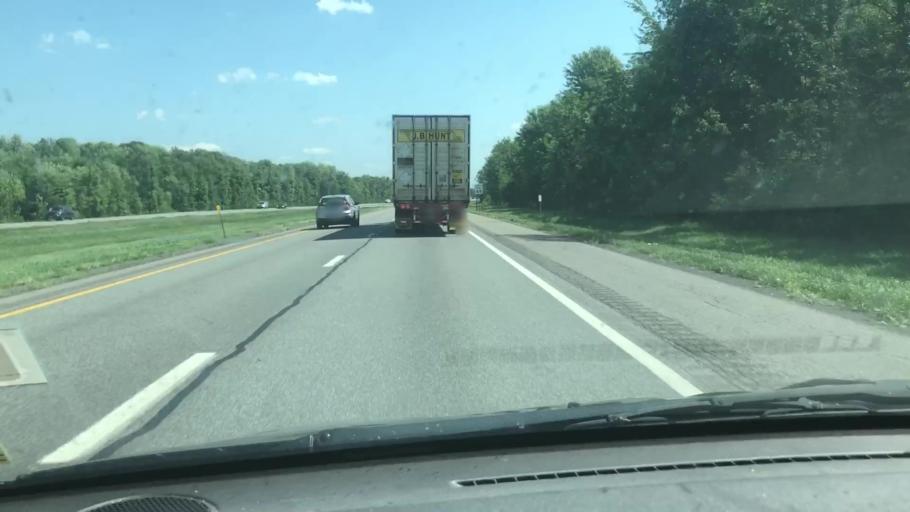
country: US
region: New York
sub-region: Madison County
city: Canastota
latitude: 43.0938
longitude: -75.8068
